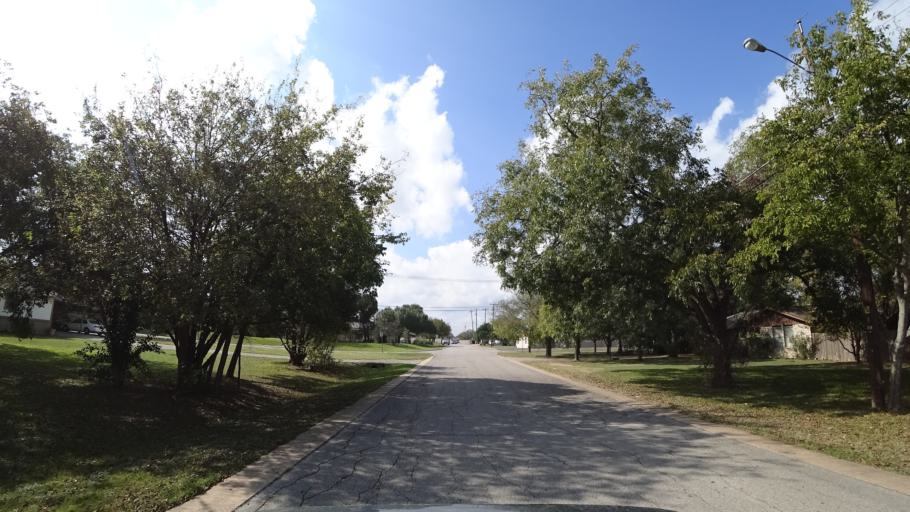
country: US
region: Texas
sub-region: Williamson County
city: Round Rock
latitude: 30.5147
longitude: -97.6846
